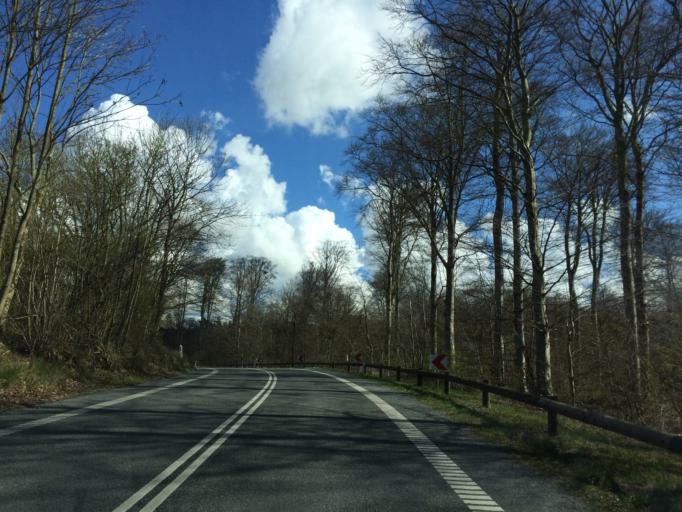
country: DK
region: South Denmark
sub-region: Assens Kommune
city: Harby
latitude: 55.1756
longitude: 10.1499
